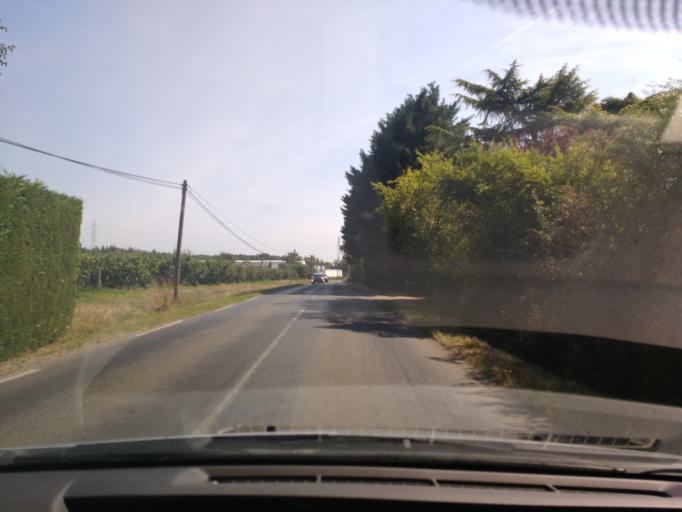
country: FR
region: Pays de la Loire
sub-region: Departement de Maine-et-Loire
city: Trelaze
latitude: 47.4696
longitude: -0.4648
